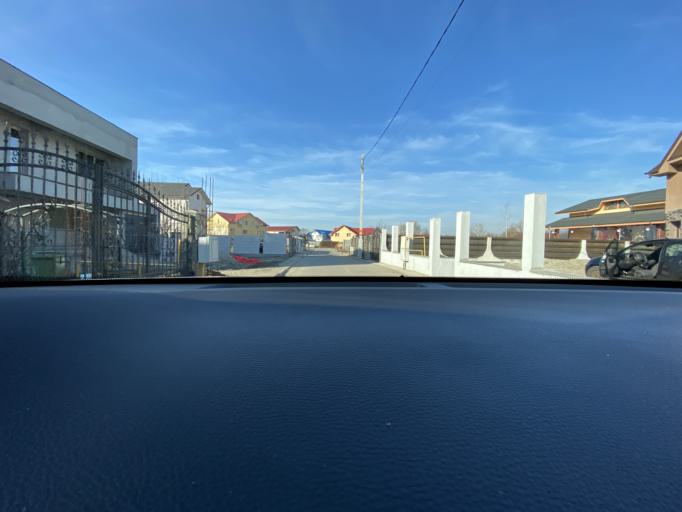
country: RO
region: Olt
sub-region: Municipiul Slatina
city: Slatina
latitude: 44.4374
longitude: 24.3746
